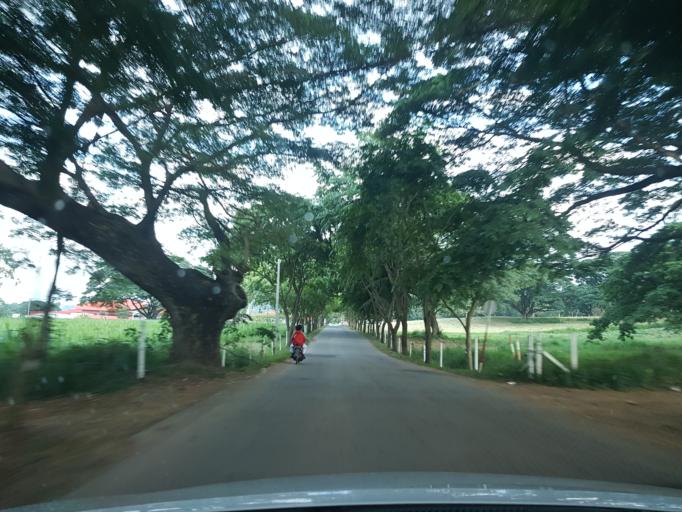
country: TH
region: Sara Buri
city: Muak Lek
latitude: 14.6311
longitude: 101.1986
